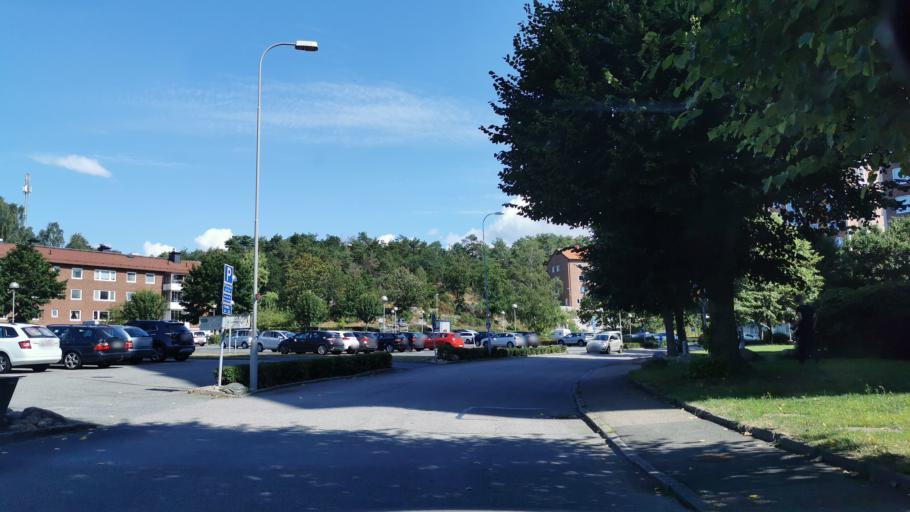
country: SE
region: Vaestra Goetaland
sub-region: Goteborg
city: Majorna
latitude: 57.6608
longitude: 11.9121
